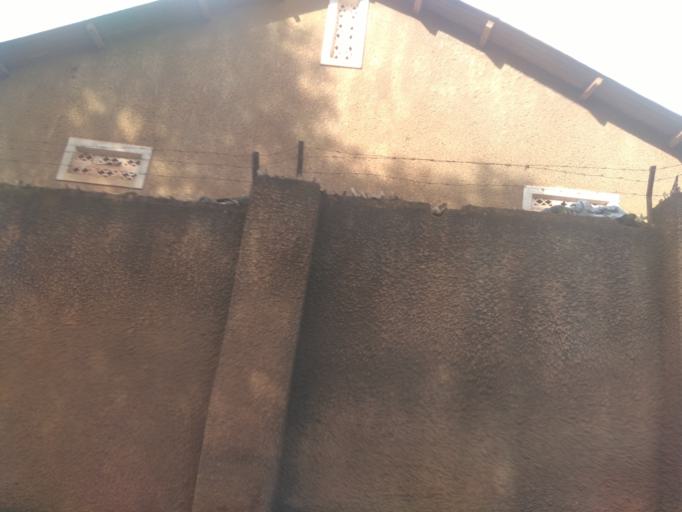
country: UG
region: Central Region
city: Kampala Central Division
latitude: 0.3589
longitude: 32.5787
